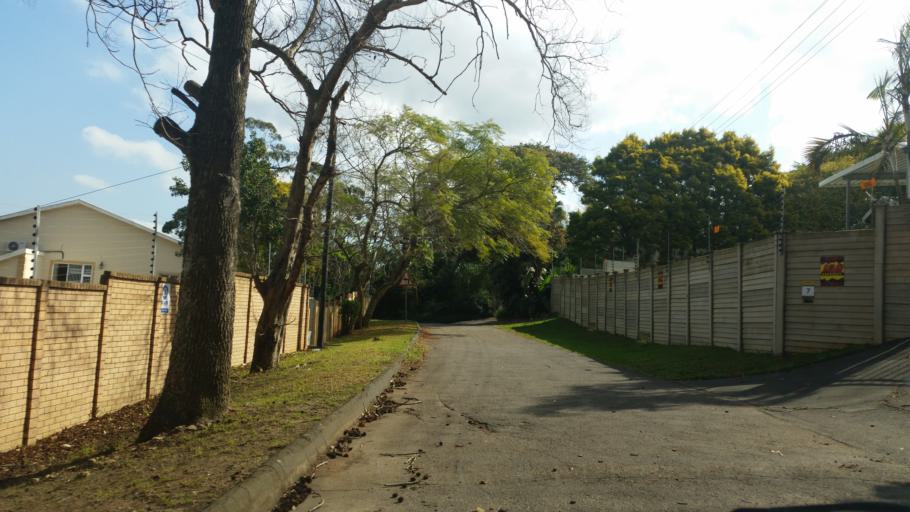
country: ZA
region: KwaZulu-Natal
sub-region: eThekwini Metropolitan Municipality
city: Berea
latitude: -29.8339
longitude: 30.8998
